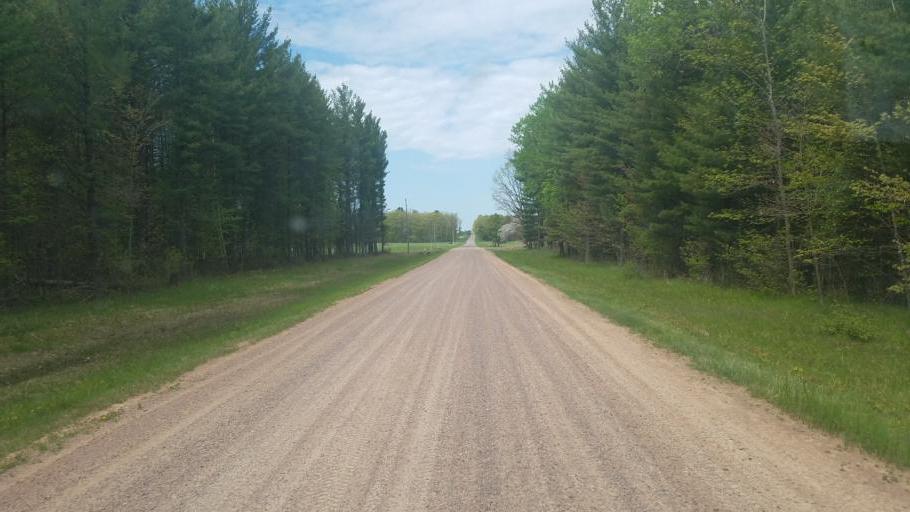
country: US
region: Wisconsin
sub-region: Clark County
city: Neillsville
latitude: 44.4732
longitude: -90.4445
